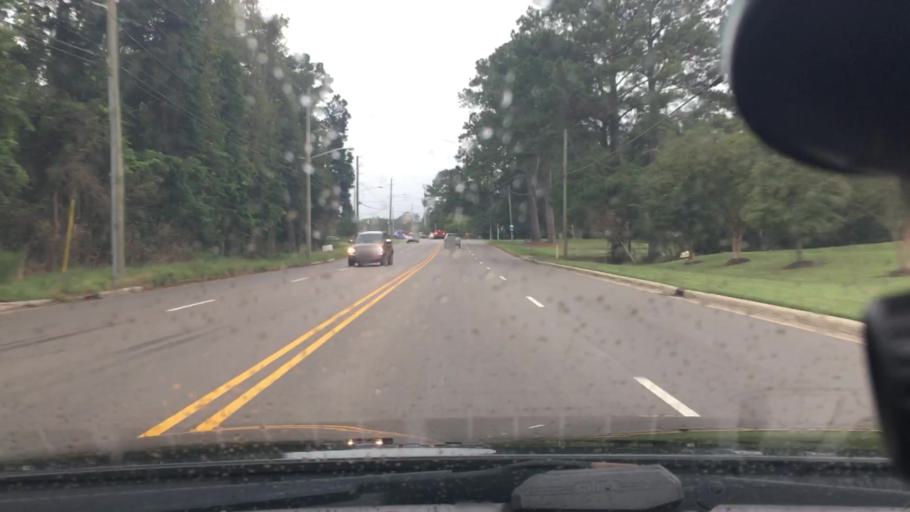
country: US
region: North Carolina
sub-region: Pitt County
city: Summerfield
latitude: 35.5968
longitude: -77.4000
